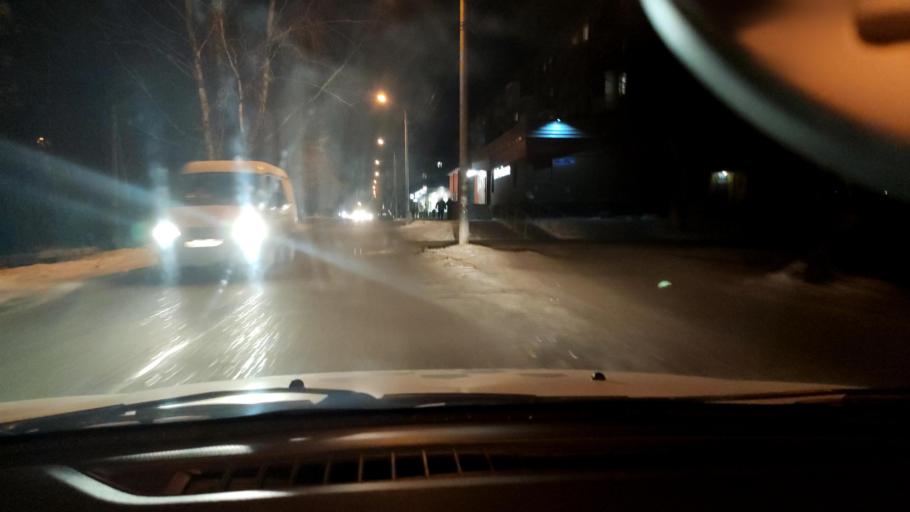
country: RU
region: Perm
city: Overyata
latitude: 58.0275
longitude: 55.8413
